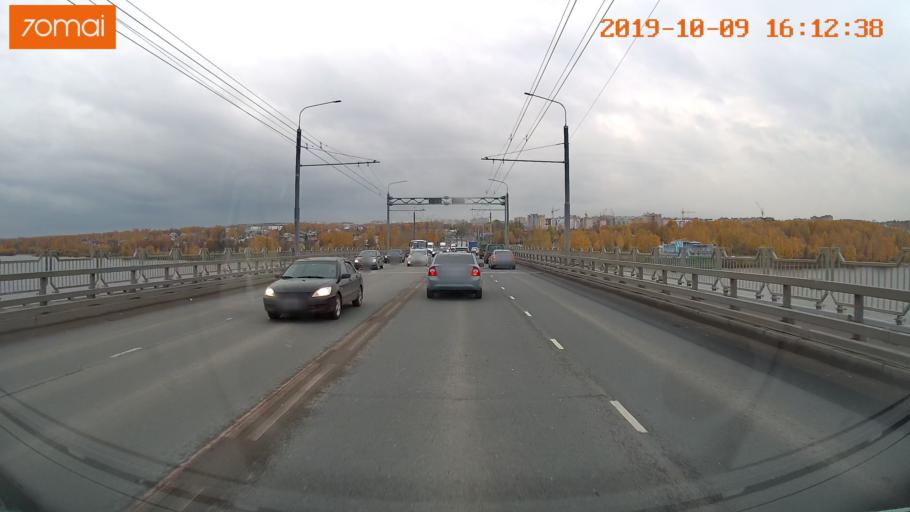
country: RU
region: Kostroma
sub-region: Kostromskoy Rayon
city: Kostroma
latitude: 57.7512
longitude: 40.9366
